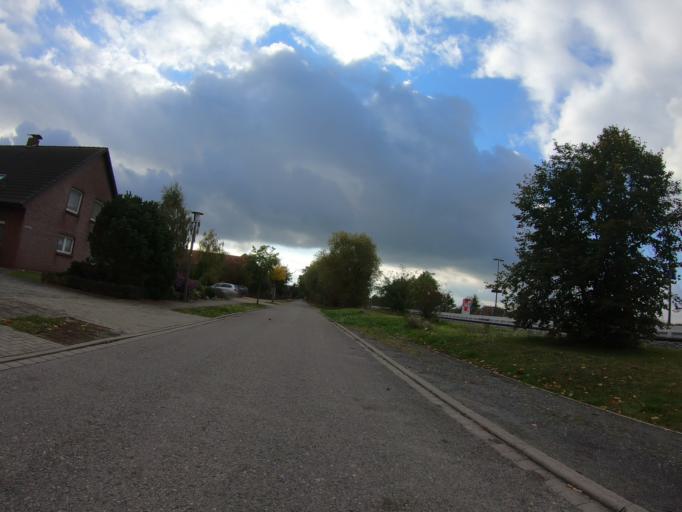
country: DE
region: Lower Saxony
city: Wahrenholz
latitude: 52.6078
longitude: 10.6072
